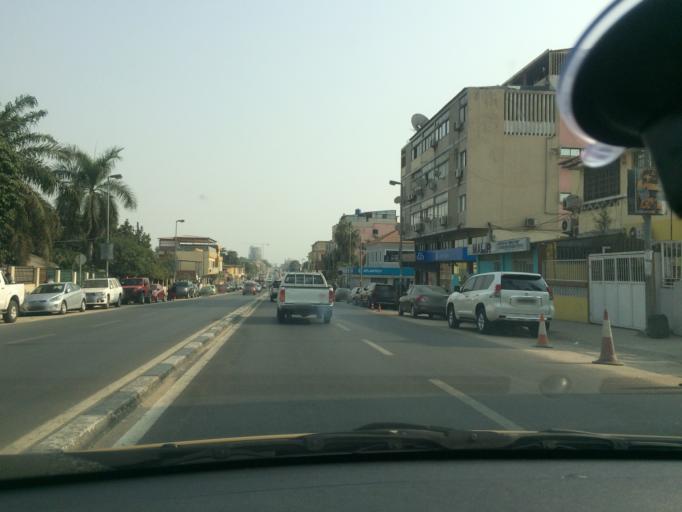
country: AO
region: Luanda
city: Luanda
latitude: -8.8273
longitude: 13.2230
